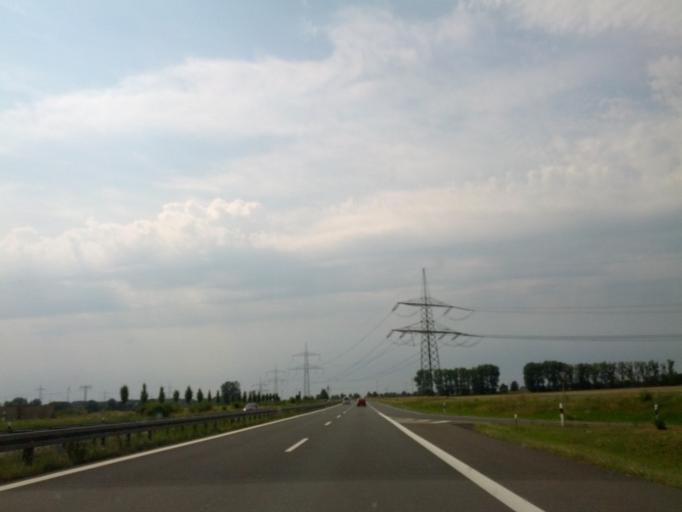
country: DE
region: Brandenburg
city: Wustermark
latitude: 52.5567
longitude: 12.9509
